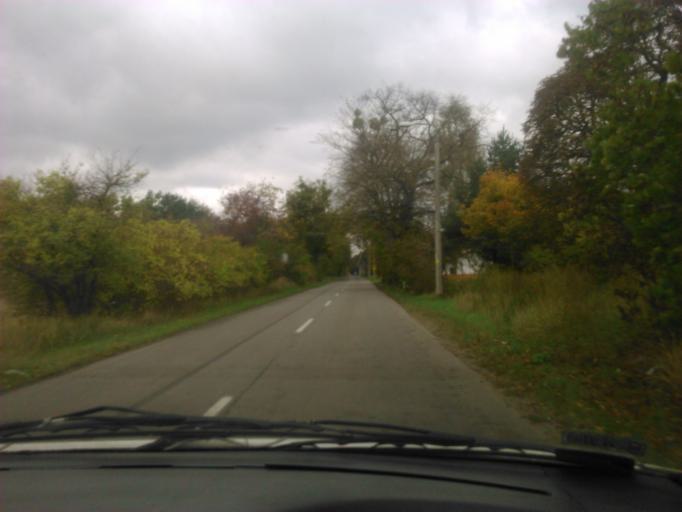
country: PL
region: Pomeranian Voivodeship
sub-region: Powiat gdanski
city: Cedry Wielkie
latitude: 54.3384
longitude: 18.9019
